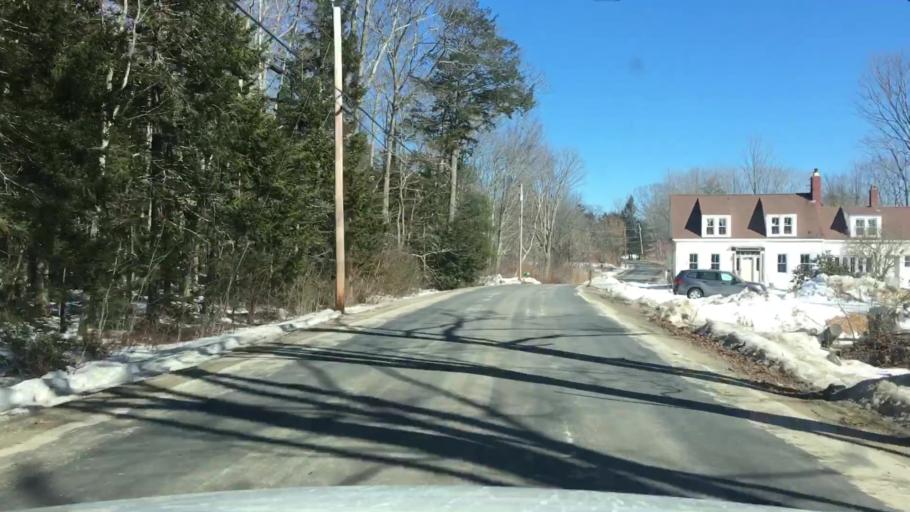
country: US
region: Maine
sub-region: Cumberland County
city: Brunswick
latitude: 43.8660
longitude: -70.0162
